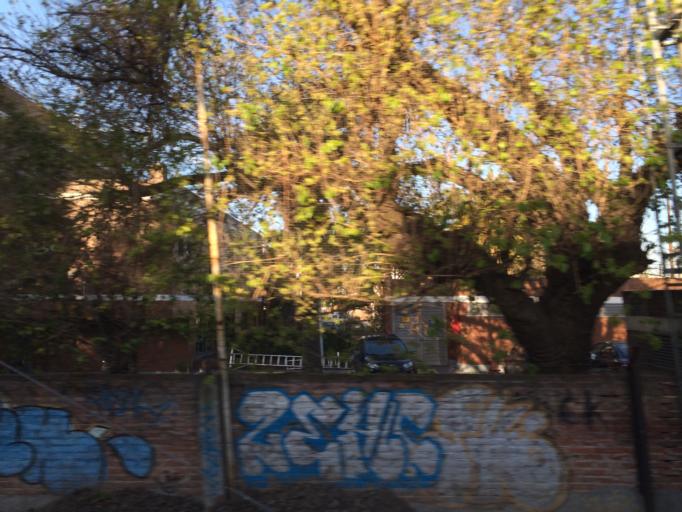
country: AR
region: Buenos Aires
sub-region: Partido de Lomas de Zamora
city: Lomas de Zamora
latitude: -34.7705
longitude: -58.3971
